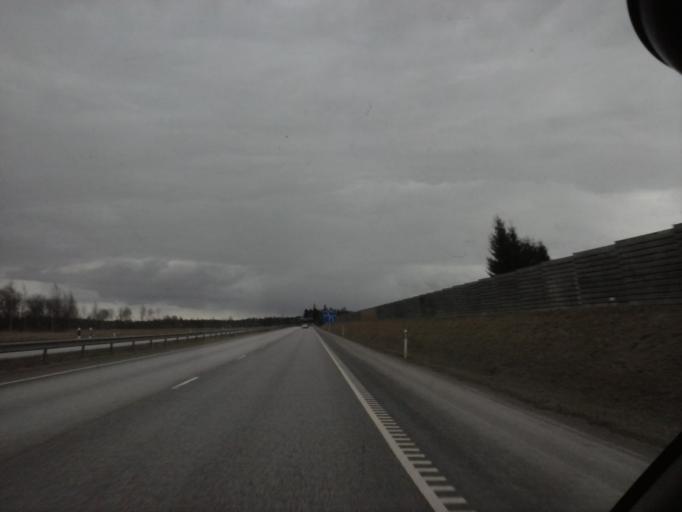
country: EE
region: Jaervamaa
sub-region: Paide linn
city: Paide
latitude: 58.9086
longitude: 25.6278
